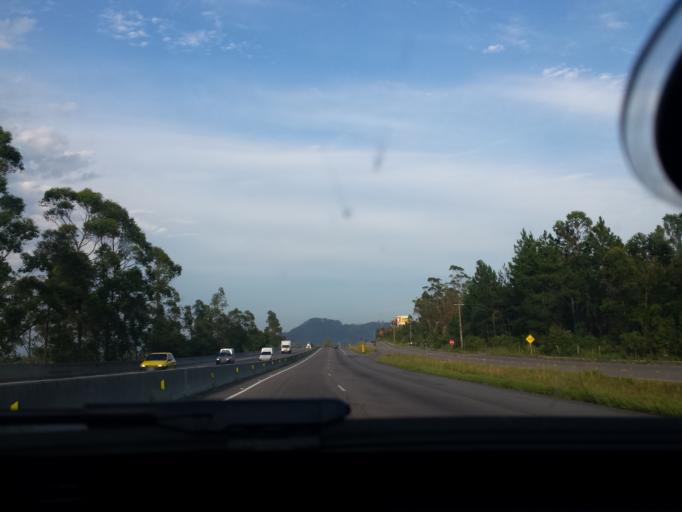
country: BR
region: Santa Catarina
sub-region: Tubarao
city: Tubarao
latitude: -28.4293
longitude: -48.9196
